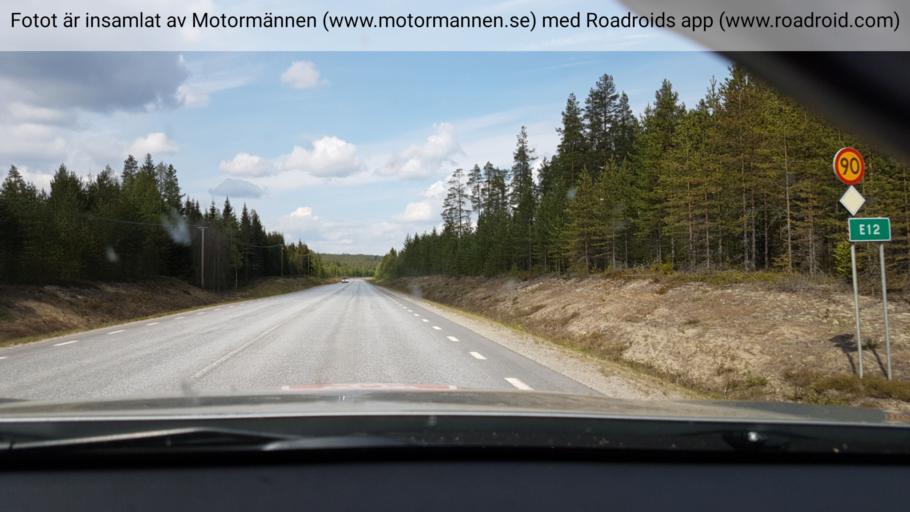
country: SE
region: Vaesterbotten
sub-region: Vannas Kommun
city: Vaennaes
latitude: 64.0149
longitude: 19.6946
